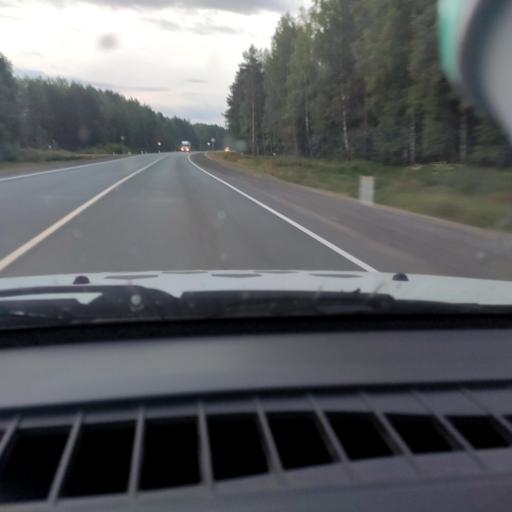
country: RU
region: Kirov
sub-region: Kirovo-Chepetskiy Rayon
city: Kirov
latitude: 58.7114
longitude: 49.5941
